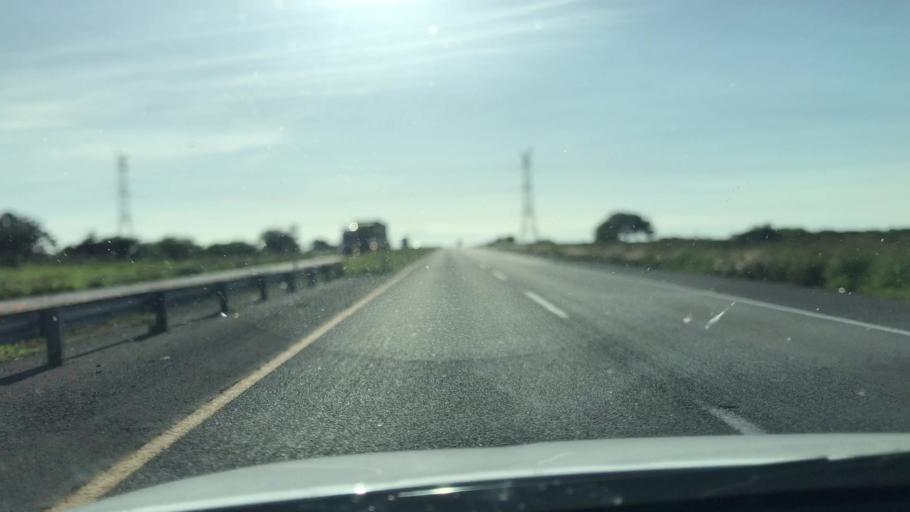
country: MX
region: Jalisco
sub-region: Lagos de Moreno
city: Cristeros [Fraccionamiento]
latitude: 21.3074
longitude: -102.0785
